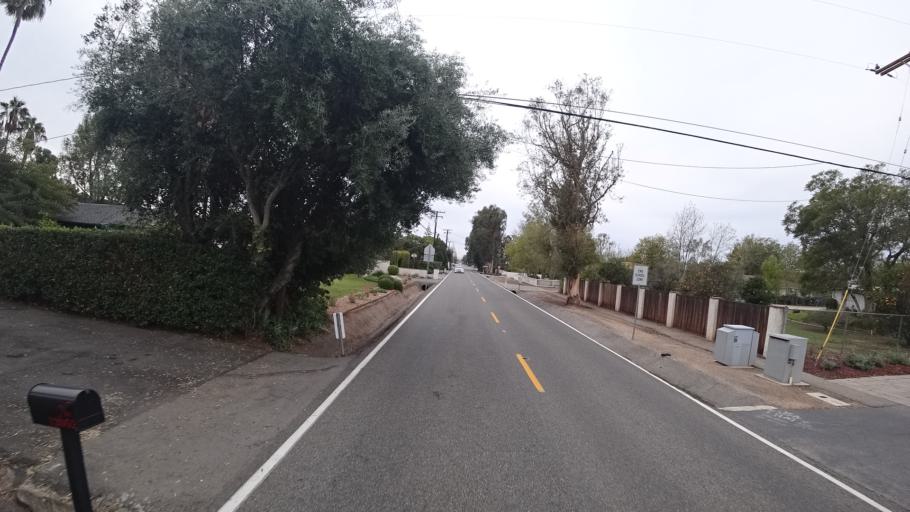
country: US
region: California
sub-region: Orange County
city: North Tustin
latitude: 33.7551
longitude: -117.7938
